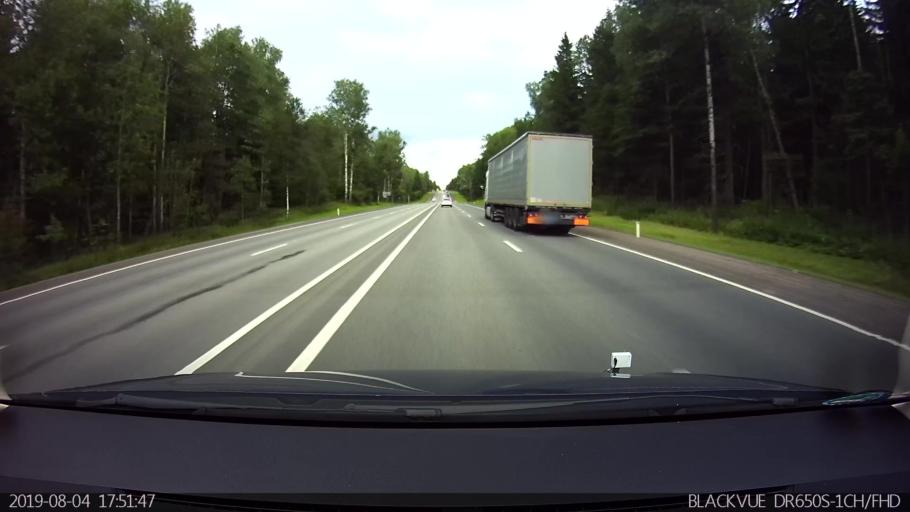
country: RU
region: Moskovskaya
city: Uvarovka
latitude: 55.4652
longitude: 35.6239
